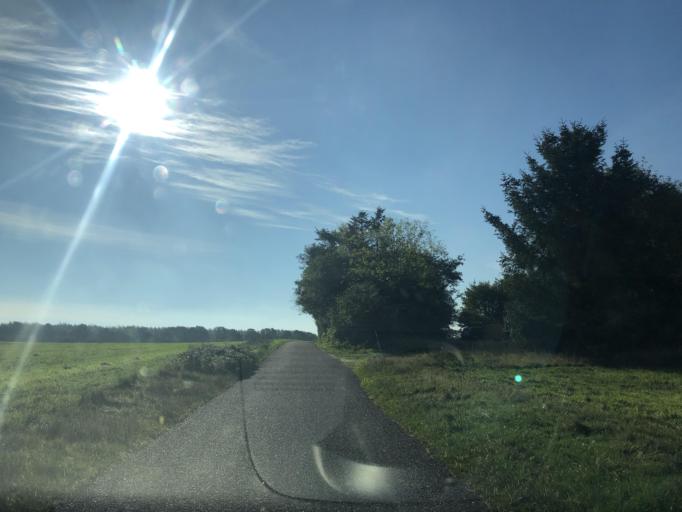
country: DK
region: Central Jutland
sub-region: Holstebro Kommune
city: Holstebro
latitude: 56.3090
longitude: 8.5050
